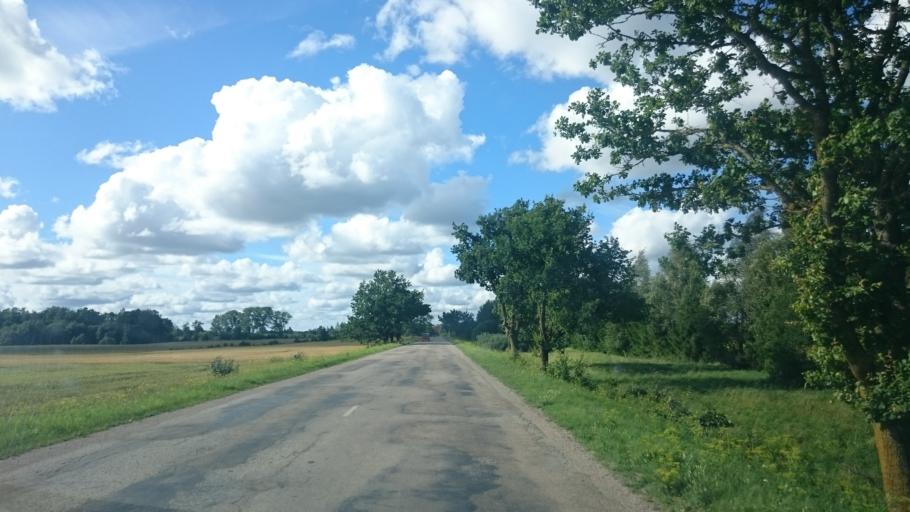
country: LV
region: Aizpute
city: Aizpute
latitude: 56.7003
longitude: 21.6292
